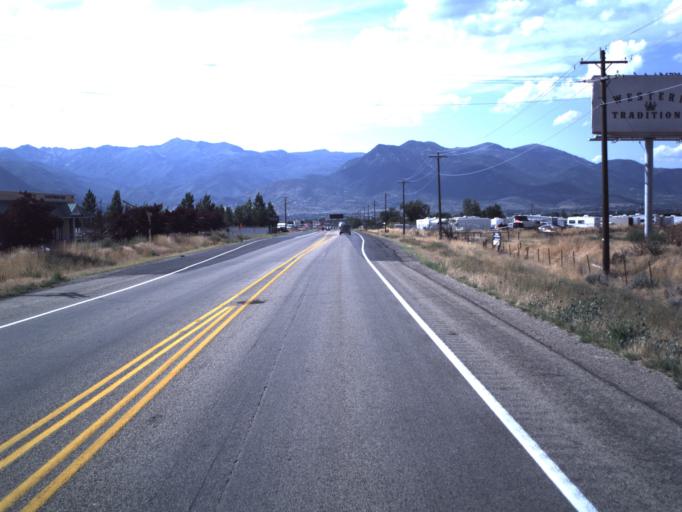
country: US
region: Utah
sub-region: Wasatch County
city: Heber
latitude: 40.4793
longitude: -111.3994
